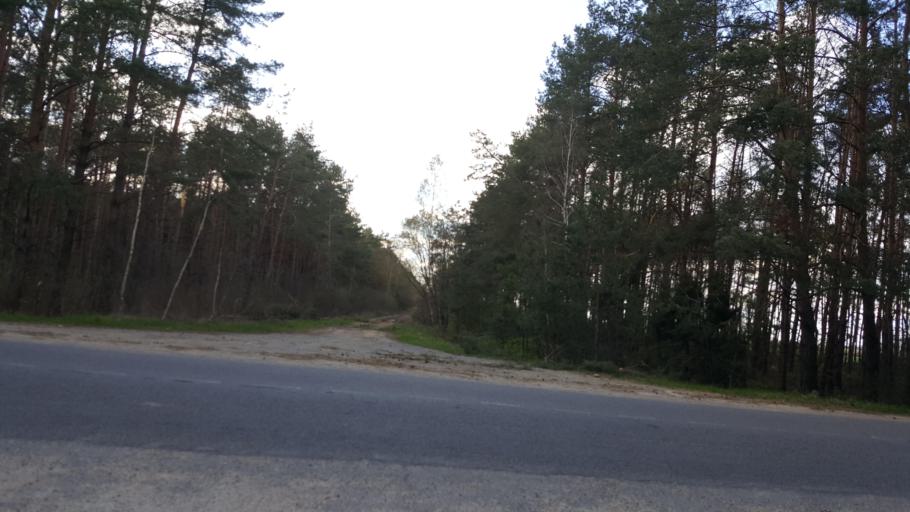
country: BY
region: Brest
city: Kamyanyets
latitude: 52.4250
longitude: 23.6430
